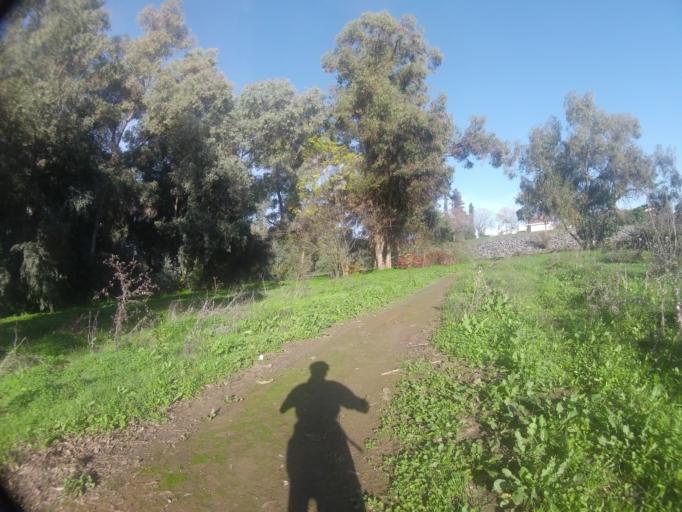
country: ES
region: Andalusia
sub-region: Provincia de Huelva
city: Gibraleon
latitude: 37.3765
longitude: -6.9765
